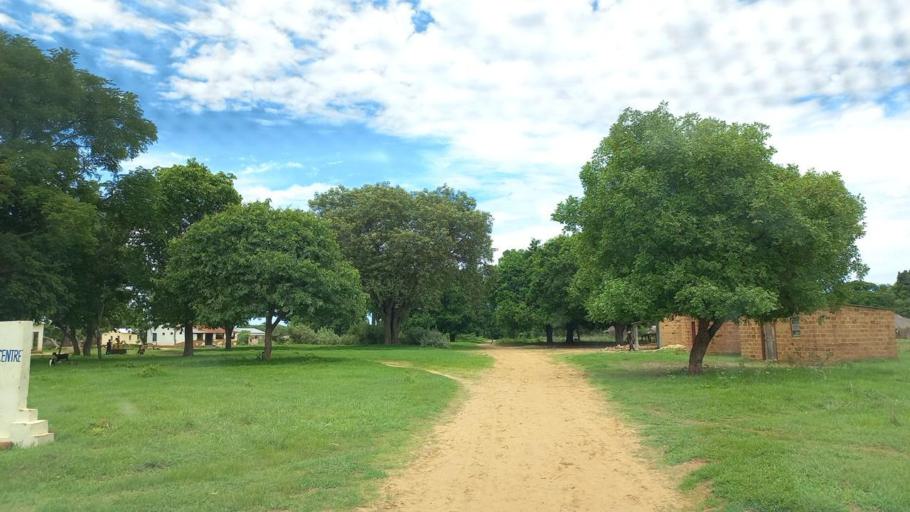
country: ZM
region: North-Western
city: Kabompo
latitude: -13.6234
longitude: 24.1857
